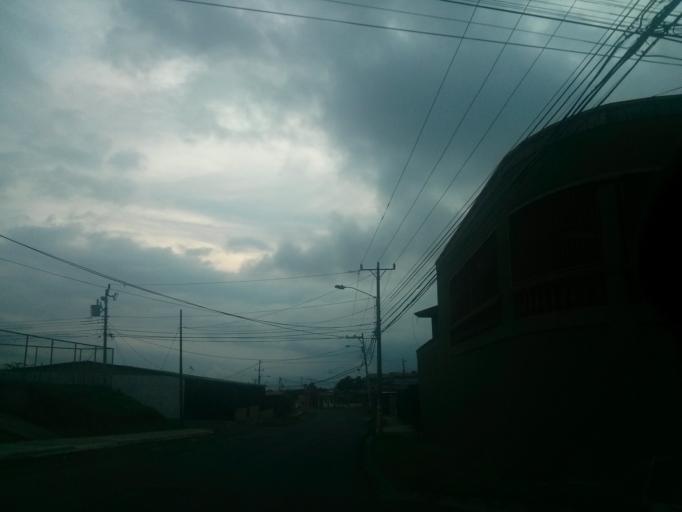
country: CR
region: Heredia
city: San Pablo
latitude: 9.9939
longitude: -84.1032
